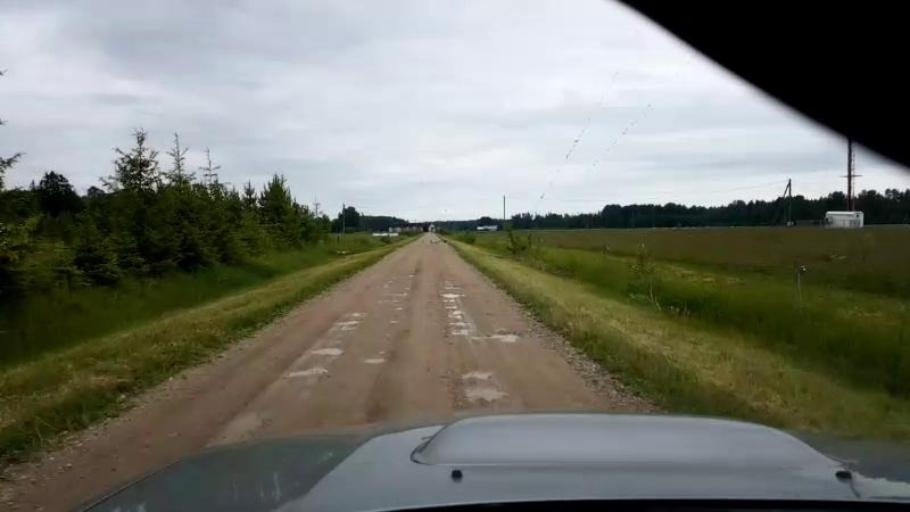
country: EE
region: Paernumaa
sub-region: Halinga vald
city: Parnu-Jaagupi
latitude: 58.5311
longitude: 24.5785
